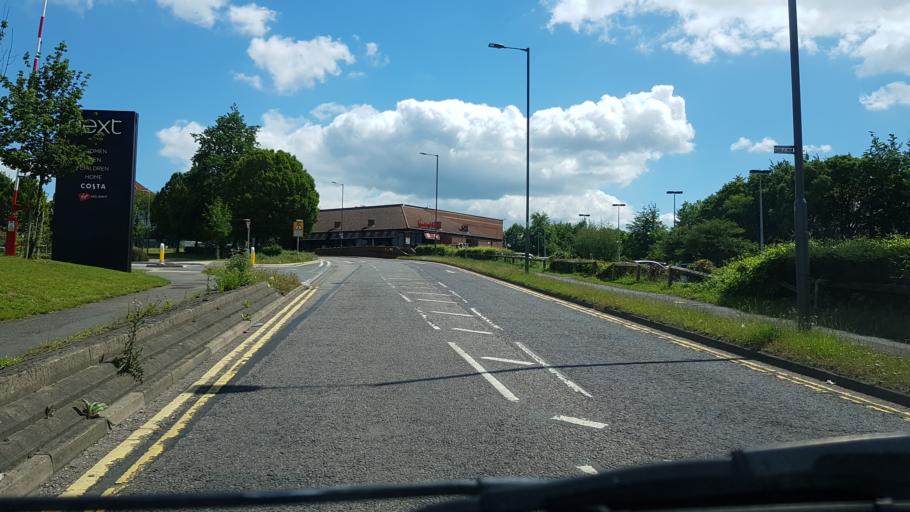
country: GB
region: England
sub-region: Buckinghamshire
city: High Wycombe
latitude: 51.6124
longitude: -0.7741
